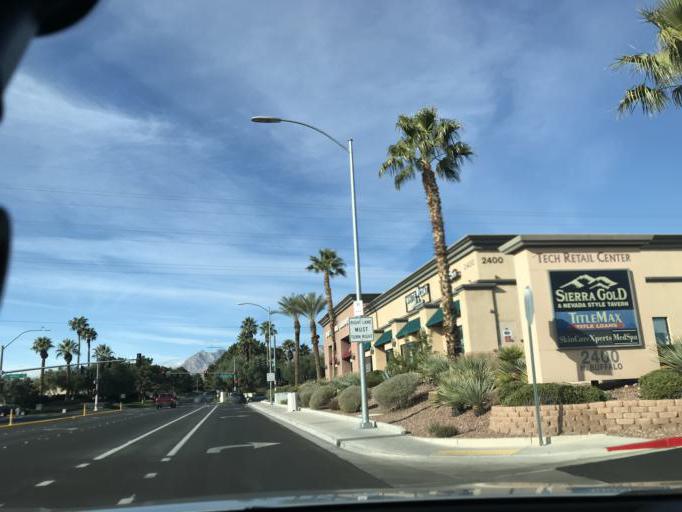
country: US
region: Nevada
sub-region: Clark County
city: Spring Valley
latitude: 36.2036
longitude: -115.2595
